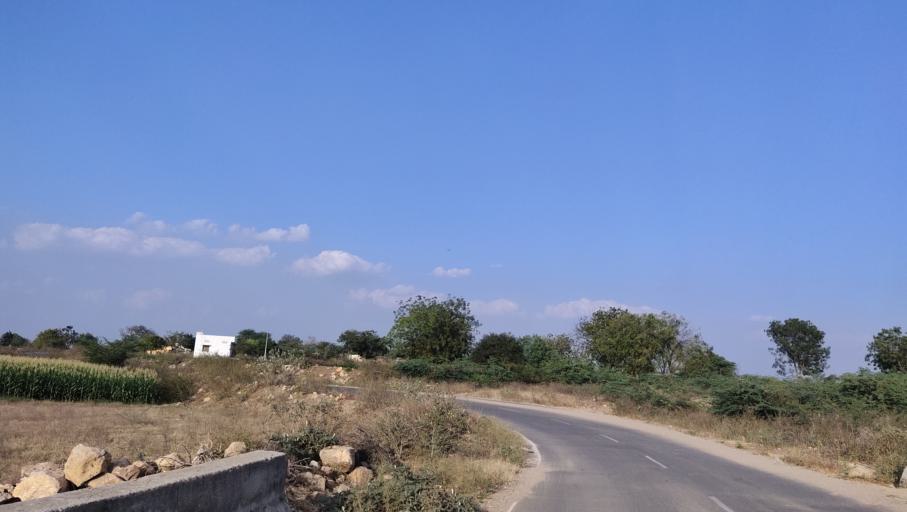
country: IN
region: Andhra Pradesh
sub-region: Anantapur
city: Tadpatri
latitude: 14.9362
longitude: 77.8656
